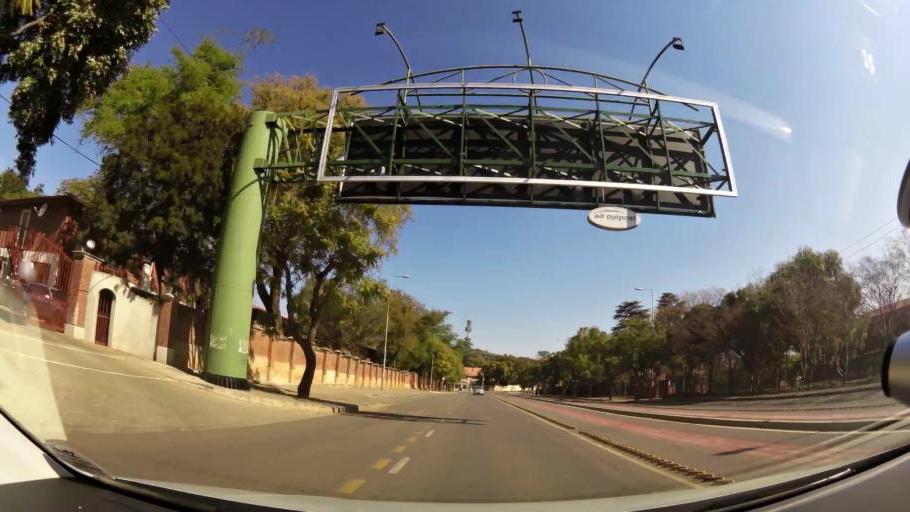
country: ZA
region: Gauteng
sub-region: City of Tshwane Metropolitan Municipality
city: Pretoria
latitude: -25.7571
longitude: 28.2200
